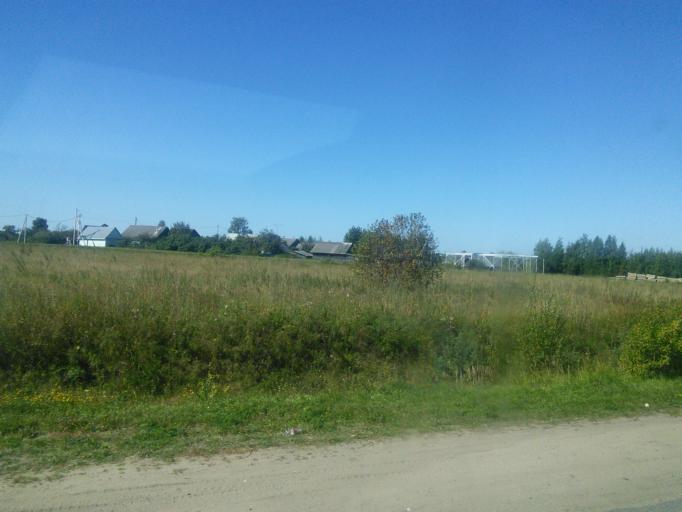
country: RU
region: Tverskaya
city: Kalyazin
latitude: 57.2128
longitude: 37.8702
